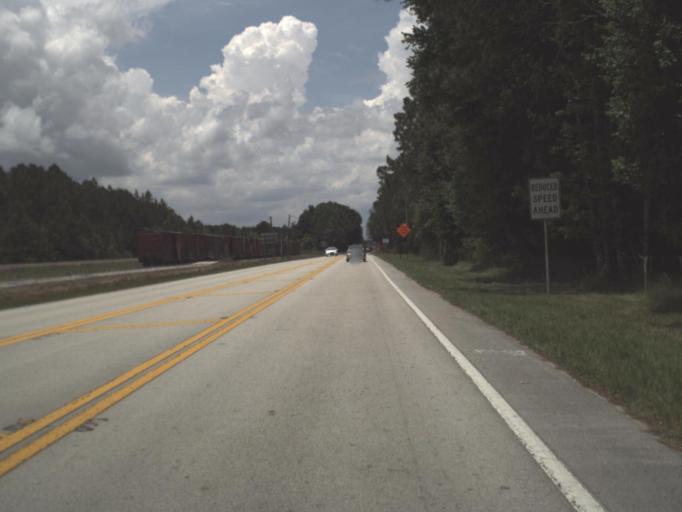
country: US
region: Florida
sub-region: Nassau County
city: Yulee
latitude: 30.7018
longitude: -81.6643
